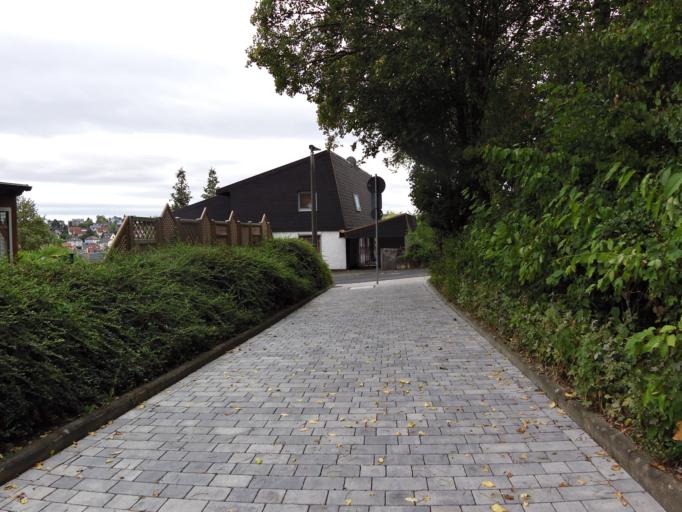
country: DE
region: Bavaria
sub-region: Regierungsbezirk Unterfranken
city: Rimpar
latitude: 49.8536
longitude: 9.9574
